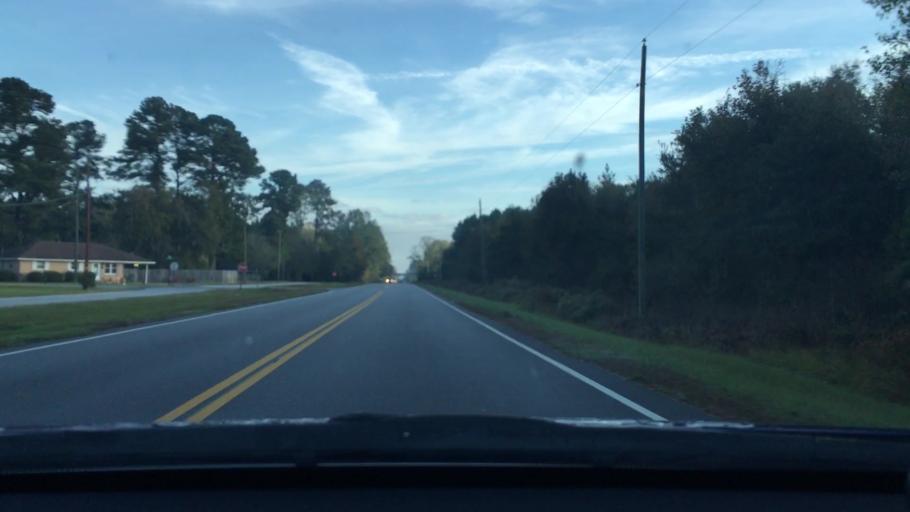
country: US
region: South Carolina
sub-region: Sumter County
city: Sumter
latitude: 33.9318
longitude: -80.3232
